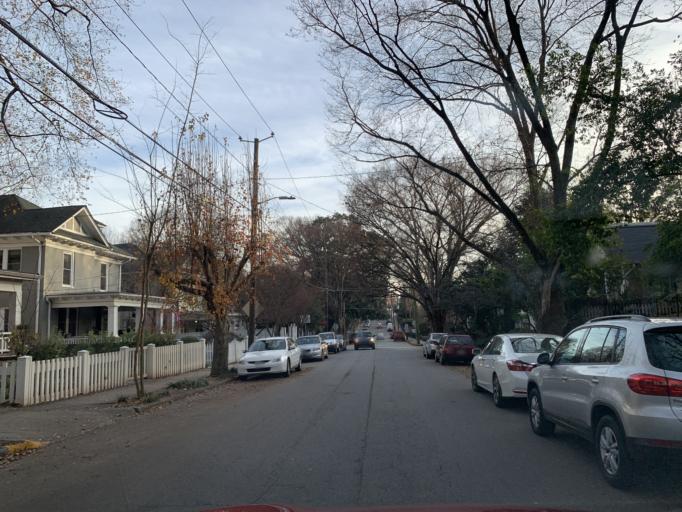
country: US
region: Georgia
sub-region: Fulton County
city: Atlanta
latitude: 33.7751
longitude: -84.3777
